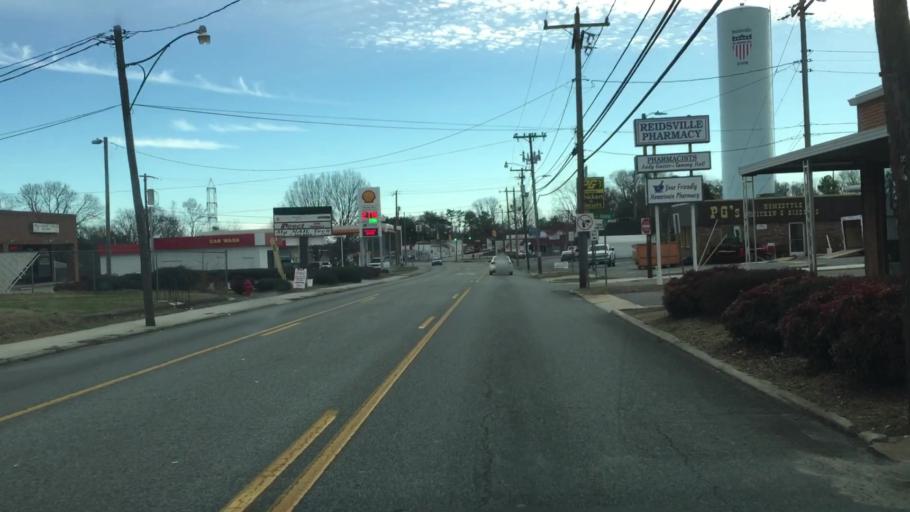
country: US
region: North Carolina
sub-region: Rockingham County
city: Reidsville
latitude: 36.3482
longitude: -79.6651
